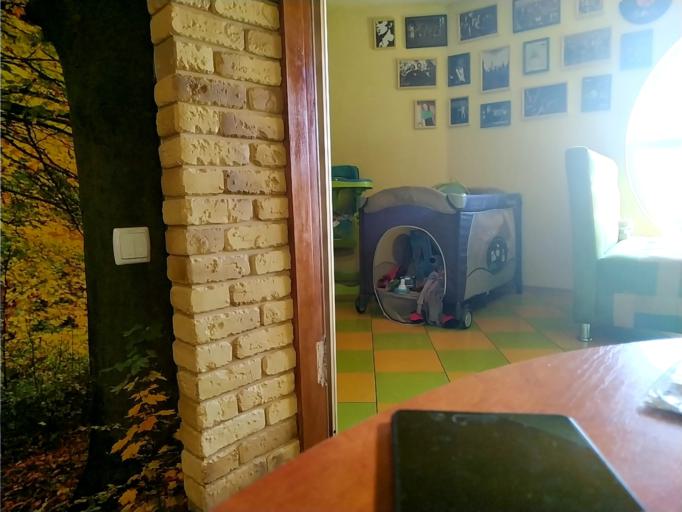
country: RU
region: Rjazan
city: Putyatino
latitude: 54.0840
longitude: 41.1589
